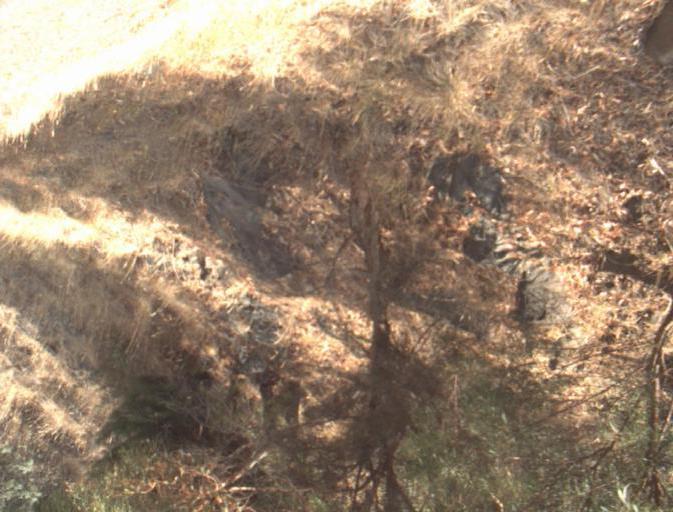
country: AU
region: Tasmania
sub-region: Launceston
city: Summerhill
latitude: -41.4798
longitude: 147.1590
